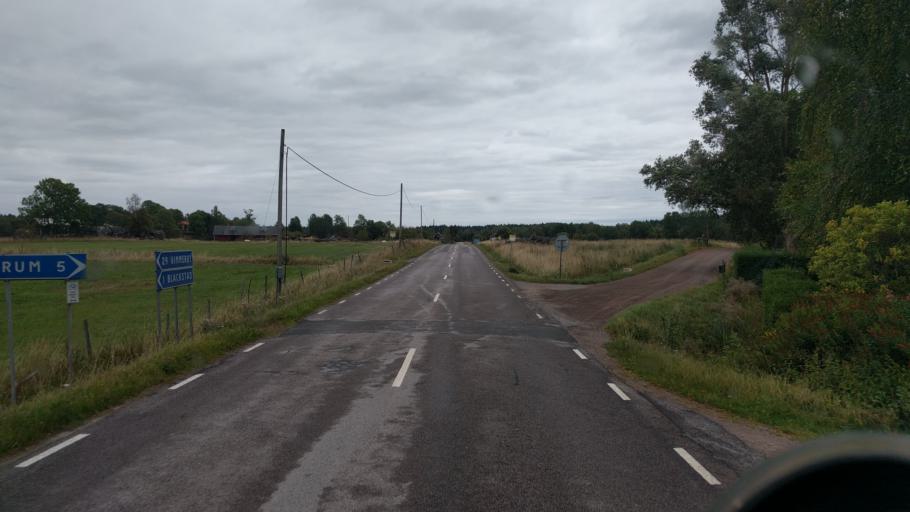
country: SE
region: Kalmar
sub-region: Vasterviks Kommun
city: Ankarsrum
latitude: 57.7859
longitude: 16.2007
